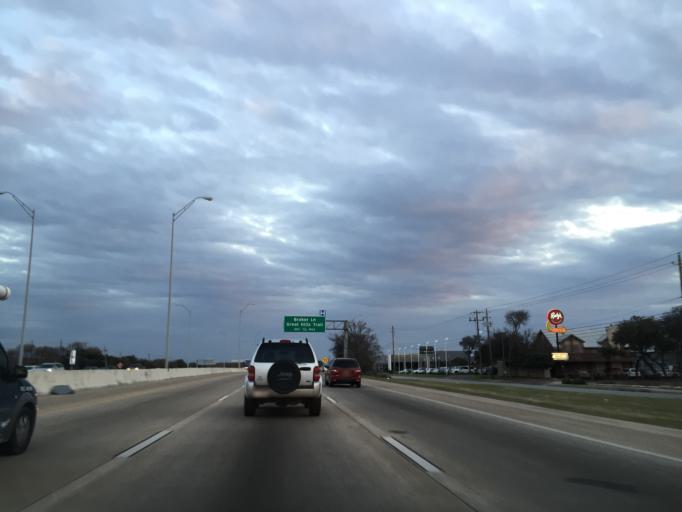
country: US
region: Texas
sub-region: Williamson County
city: Jollyville
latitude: 30.4149
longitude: -97.7463
